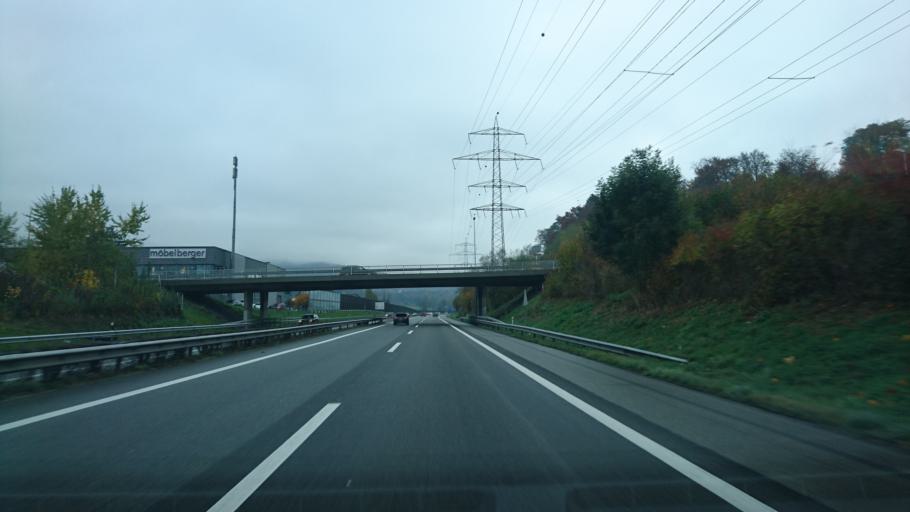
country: CH
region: Aargau
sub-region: Bezirk Zofingen
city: Oftringen
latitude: 47.3112
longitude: 7.9361
